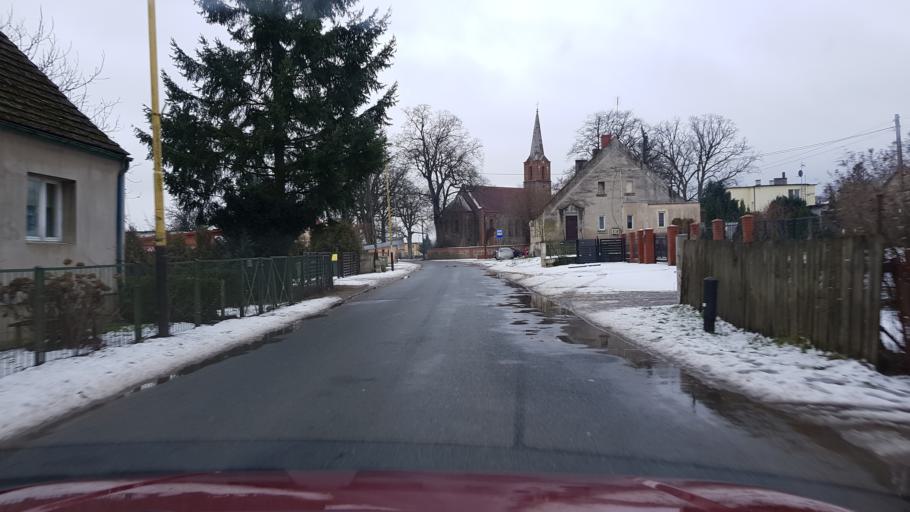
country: PL
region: West Pomeranian Voivodeship
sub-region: Powiat goleniowski
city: Nowogard
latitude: 53.6635
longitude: 15.1859
